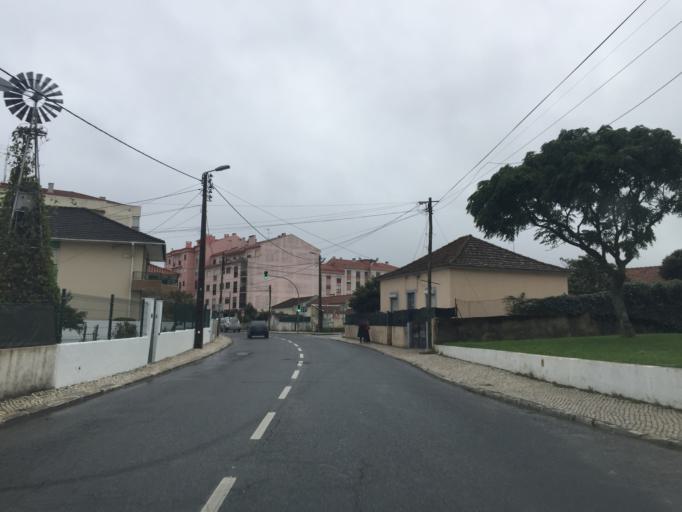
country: PT
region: Lisbon
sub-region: Sintra
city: Rio de Mouro
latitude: 38.7897
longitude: -9.3466
